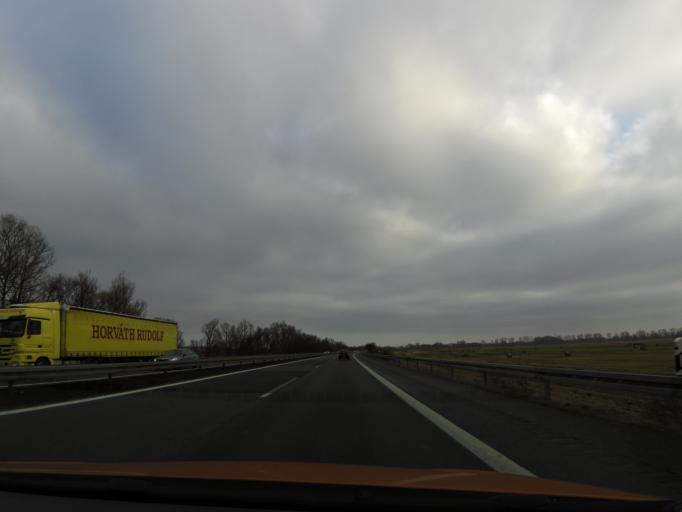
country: DE
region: Brandenburg
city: Fehrbellin
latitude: 52.8355
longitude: 12.7907
